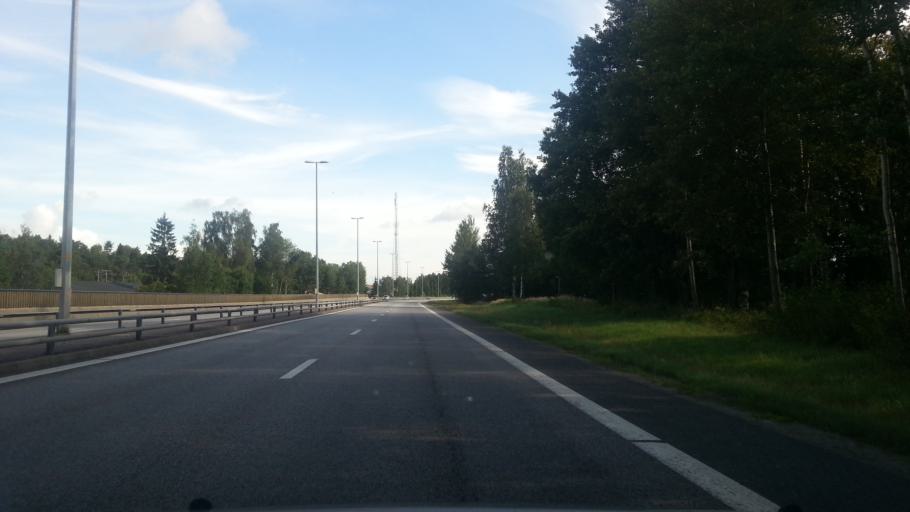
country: SE
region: Vaestra Goetaland
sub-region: Trollhattan
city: Trollhattan
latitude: 58.2742
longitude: 12.2991
